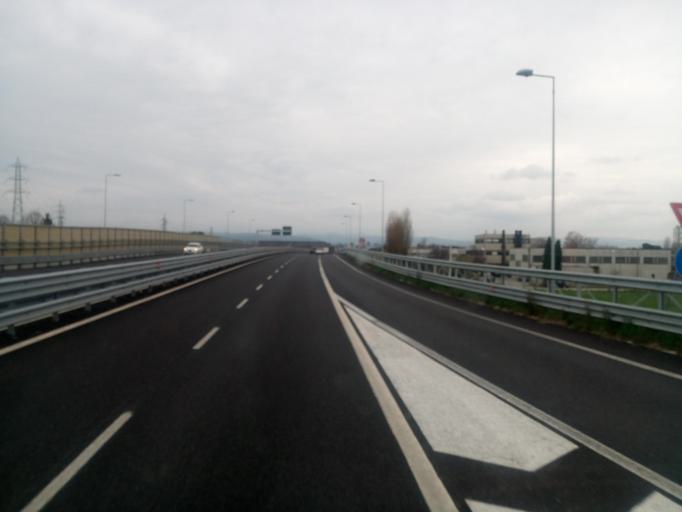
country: IT
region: Emilia-Romagna
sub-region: Forli-Cesena
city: Forli
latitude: 44.2269
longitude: 12.0887
